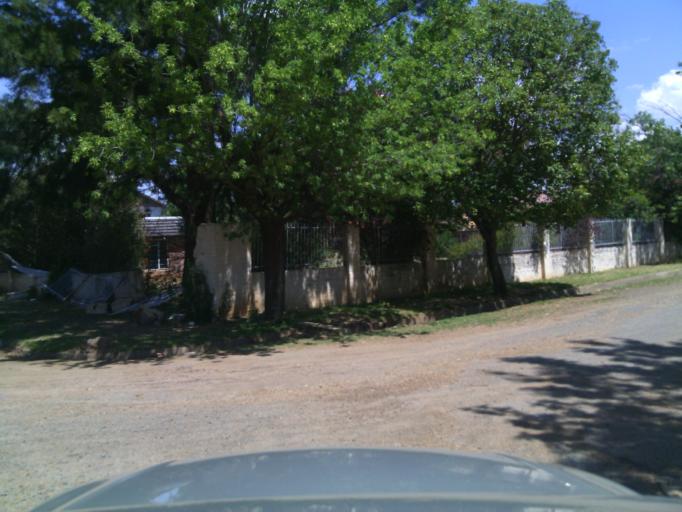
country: ZA
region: Orange Free State
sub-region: Xhariep District Municipality
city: Dewetsdorp
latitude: -29.5796
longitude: 26.6689
